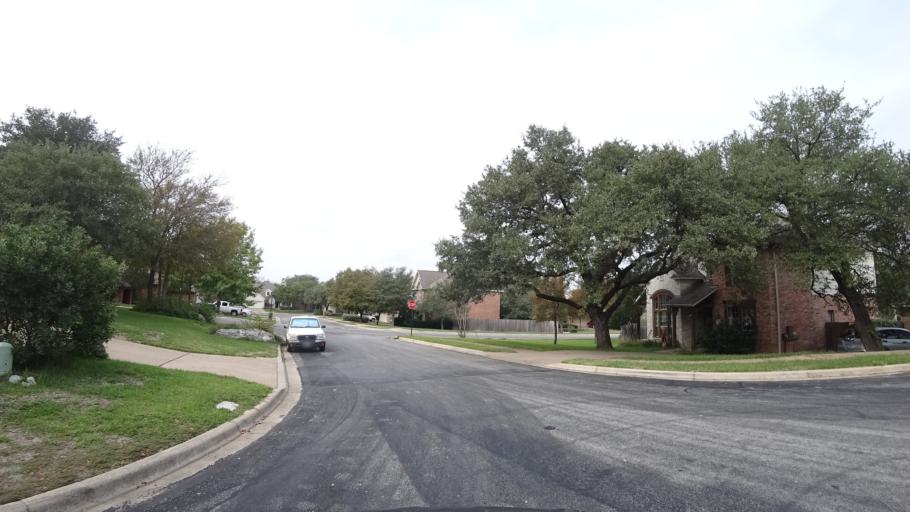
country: US
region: Texas
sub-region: Travis County
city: Shady Hollow
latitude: 30.1934
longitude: -97.8931
